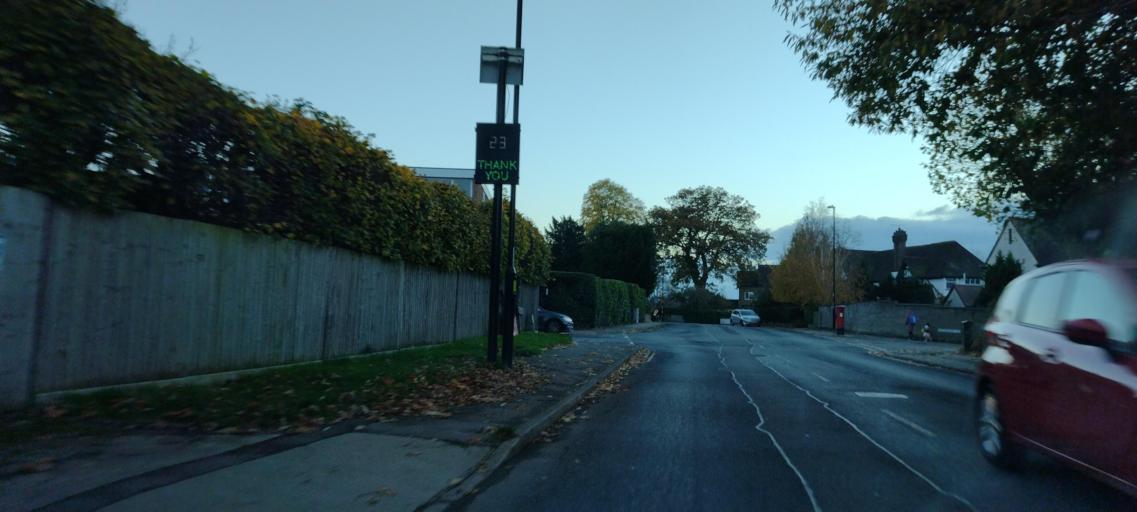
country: GB
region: England
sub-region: Coventry
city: Coventry
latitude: 52.3973
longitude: -1.5384
